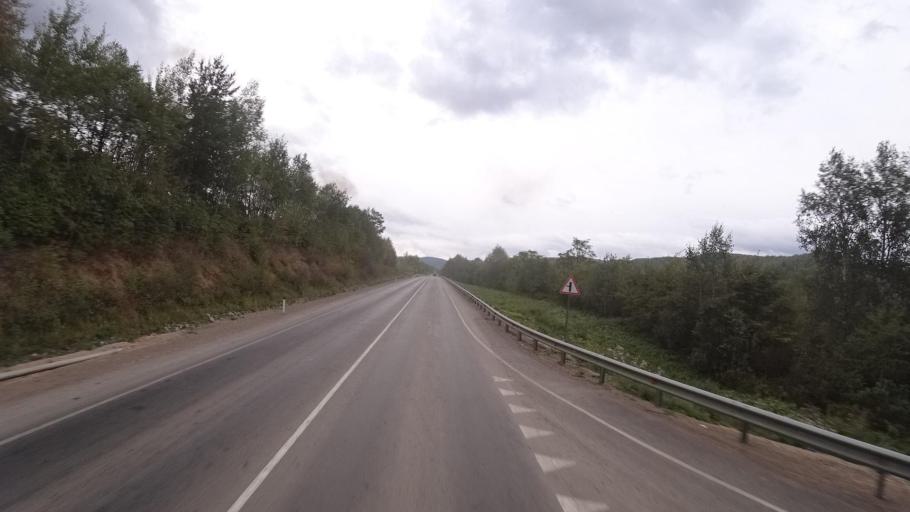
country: RU
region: Jewish Autonomous Oblast
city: Khingansk
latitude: 48.9902
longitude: 131.1227
